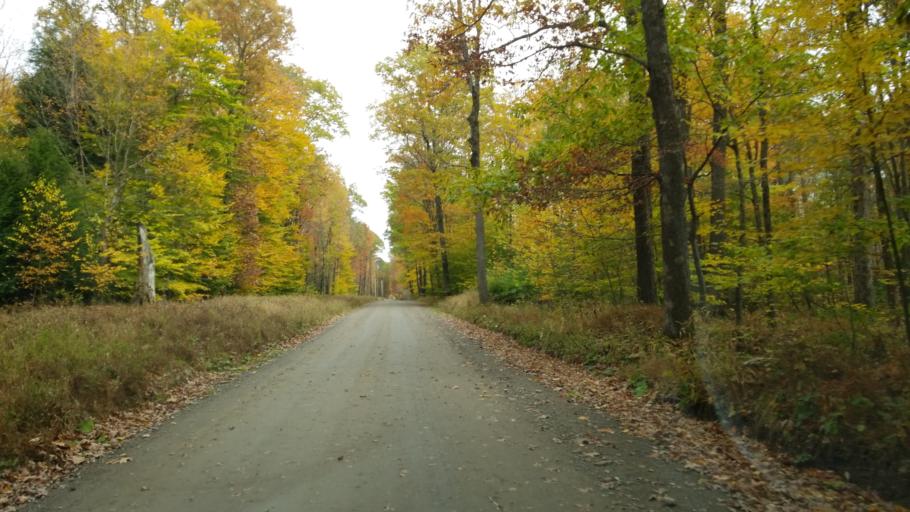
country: US
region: Pennsylvania
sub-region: Clearfield County
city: Shiloh
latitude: 41.1887
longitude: -78.3688
